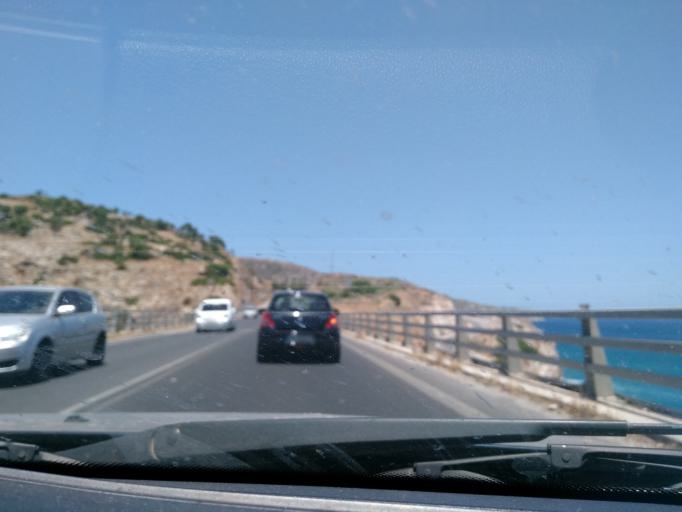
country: GR
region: Crete
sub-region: Nomos Irakleiou
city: Gazi
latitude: 35.3656
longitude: 25.0386
